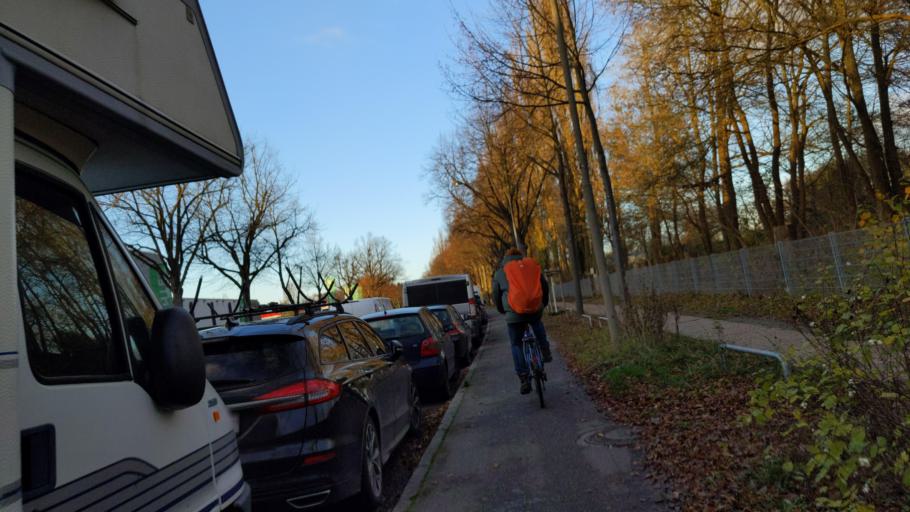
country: DE
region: Schleswig-Holstein
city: Luebeck
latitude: 53.8699
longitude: 10.6993
